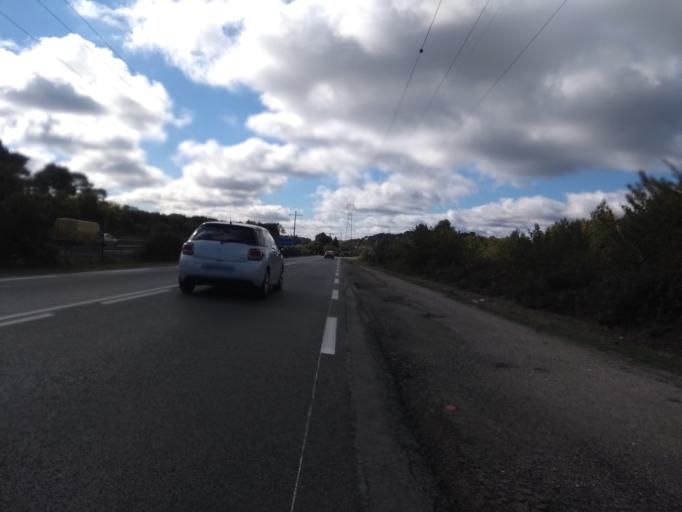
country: FR
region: Aquitaine
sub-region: Departement de la Gironde
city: Cestas
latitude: 44.7612
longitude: -0.6791
